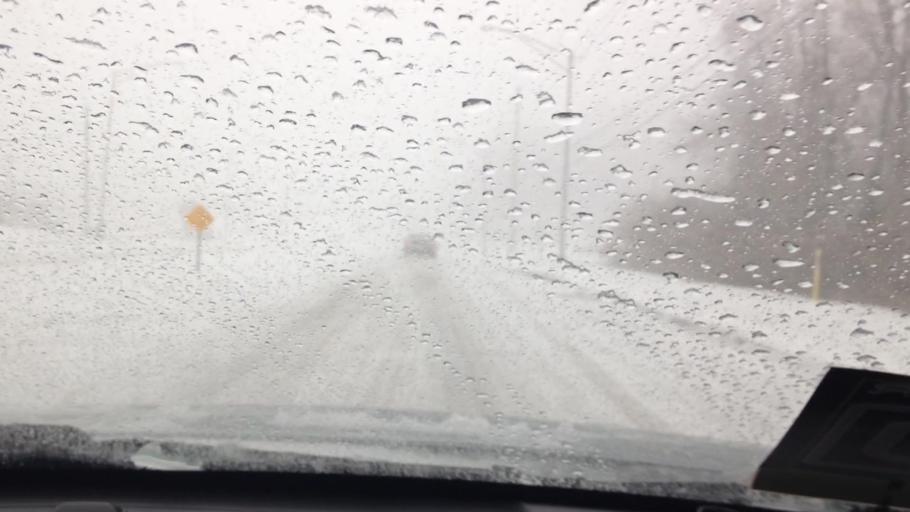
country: US
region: Kansas
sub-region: Wyandotte County
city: Kansas City
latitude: 39.1166
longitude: -94.7007
